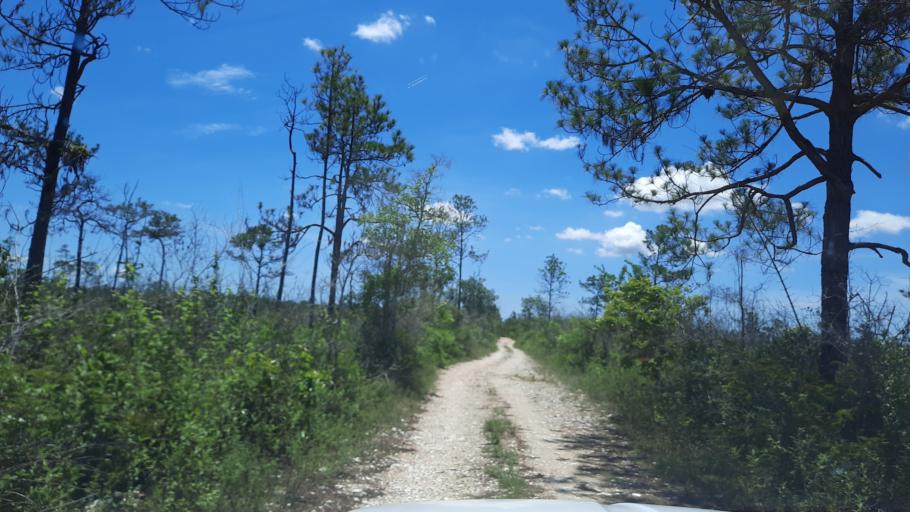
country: BZ
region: Cayo
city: Belmopan
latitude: 17.3550
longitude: -88.5473
